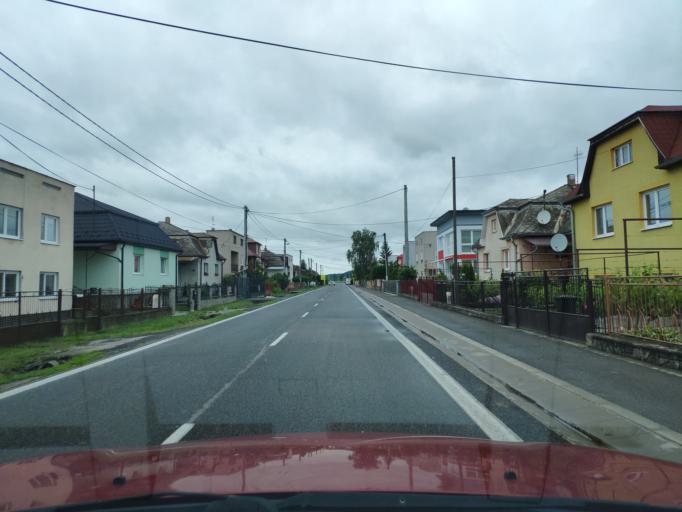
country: HU
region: Borsod-Abauj-Zemplen
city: Satoraljaujhely
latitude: 48.4091
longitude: 21.6681
